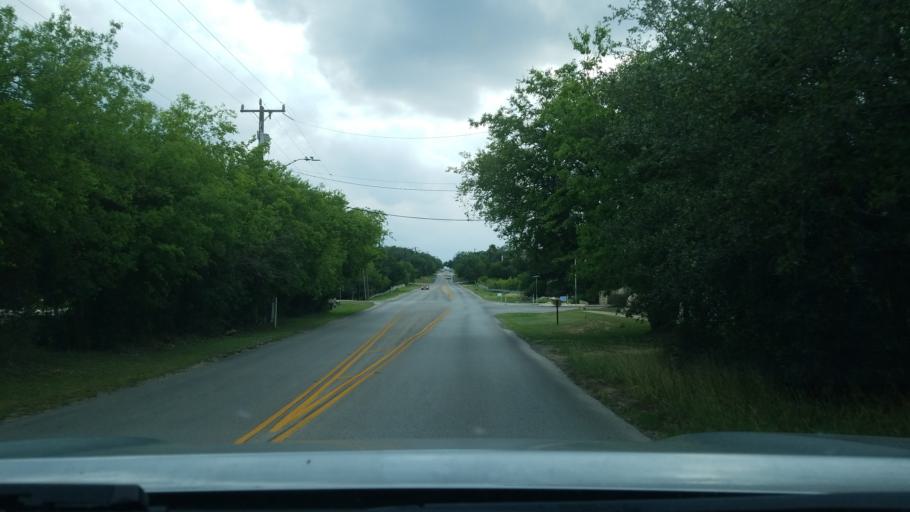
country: US
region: Texas
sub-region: Bexar County
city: Leon Valley
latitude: 29.5447
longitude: -98.6039
